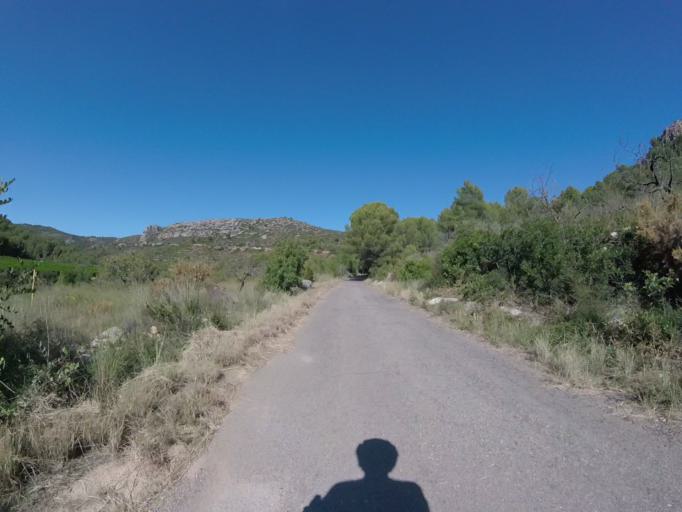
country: ES
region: Valencia
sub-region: Provincia de Castello
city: Orpesa/Oropesa del Mar
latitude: 40.1381
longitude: 0.1028
